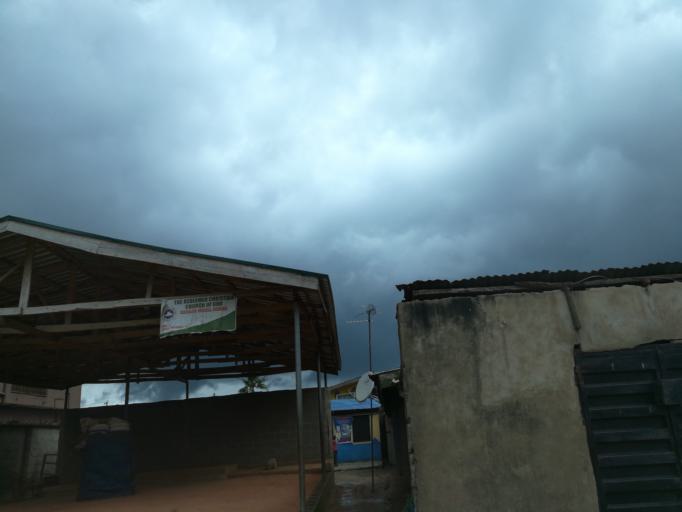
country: NG
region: Lagos
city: Agege
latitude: 6.6060
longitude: 3.3033
